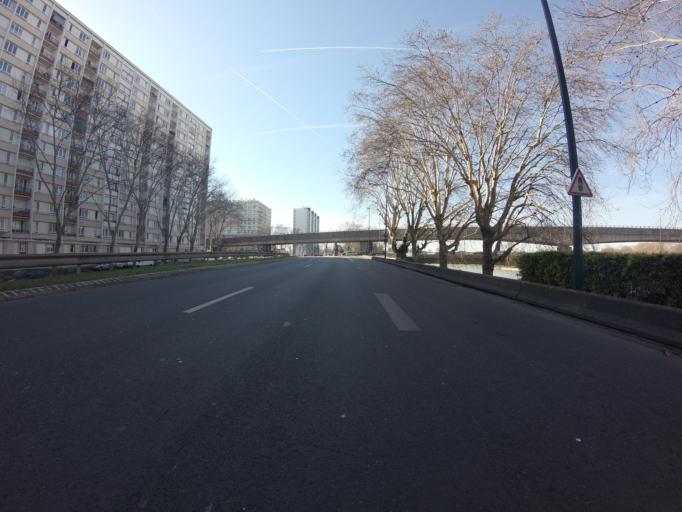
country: FR
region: Ile-de-France
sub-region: Departement des Hauts-de-Seine
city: Clichy
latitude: 48.9091
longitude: 2.3009
